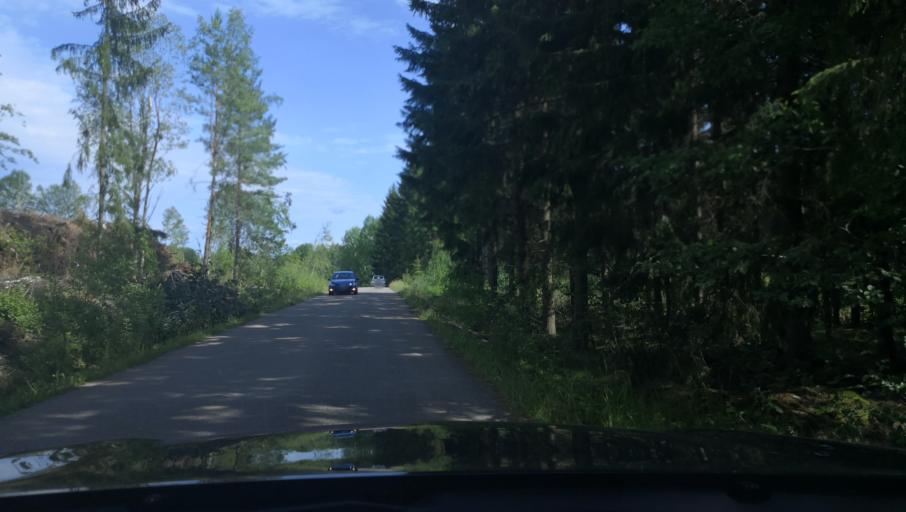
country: SE
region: Vaestmanland
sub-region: Surahammars Kommun
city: Ramnas
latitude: 59.9482
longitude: 16.2106
